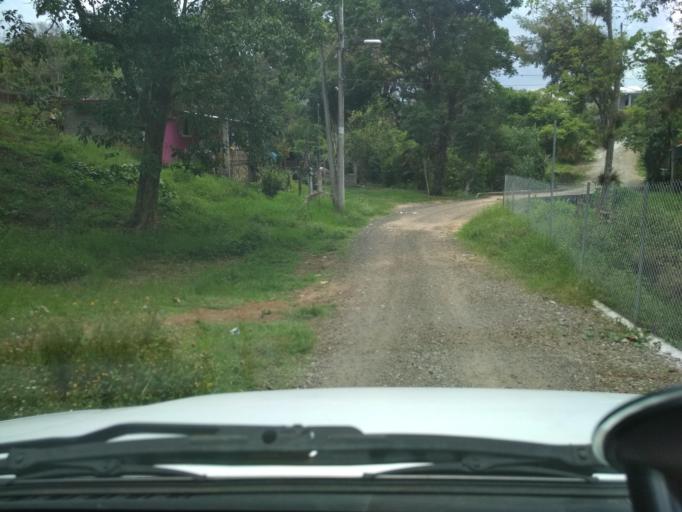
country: MX
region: Veracruz
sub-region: Cordoba
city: San Jose de Abajo [Unidad Habitacional]
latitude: 18.9195
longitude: -96.9582
